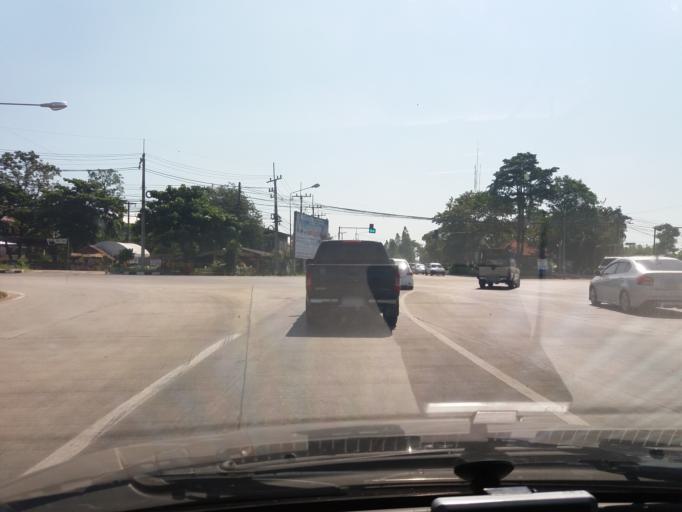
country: TH
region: Chai Nat
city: Sankhaburi
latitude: 15.0448
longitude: 100.1490
